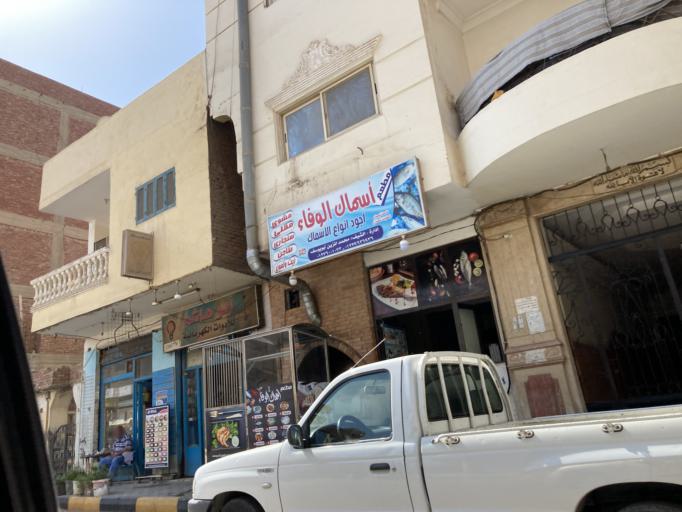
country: EG
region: Red Sea
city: Hurghada
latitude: 27.2516
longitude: 33.8311
